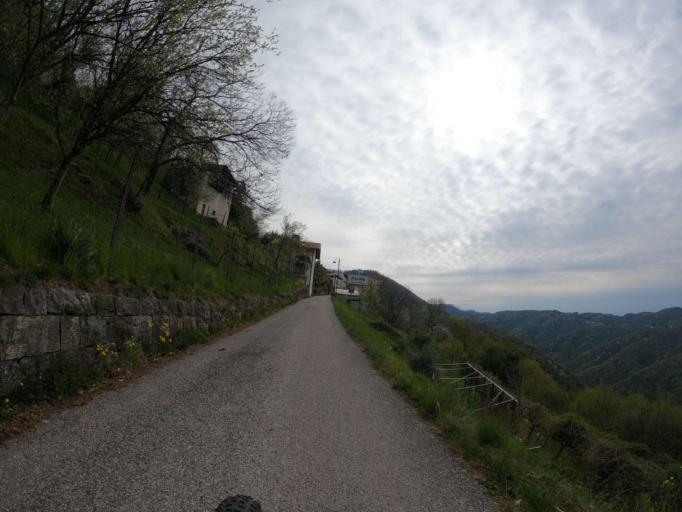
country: IT
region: Friuli Venezia Giulia
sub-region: Provincia di Udine
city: Stregna
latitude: 46.1403
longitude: 13.5777
